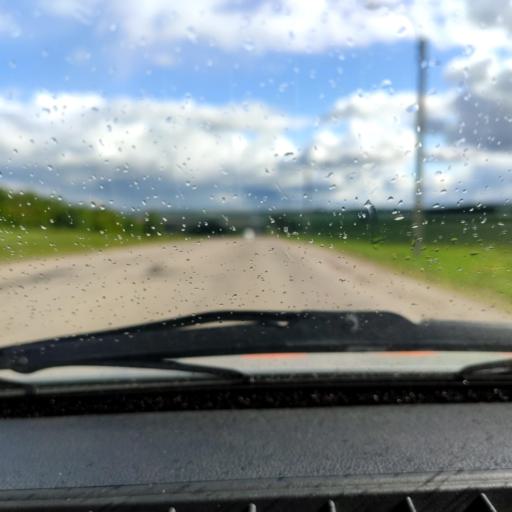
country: RU
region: Bashkortostan
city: Tolbazy
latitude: 53.9753
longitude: 55.9112
